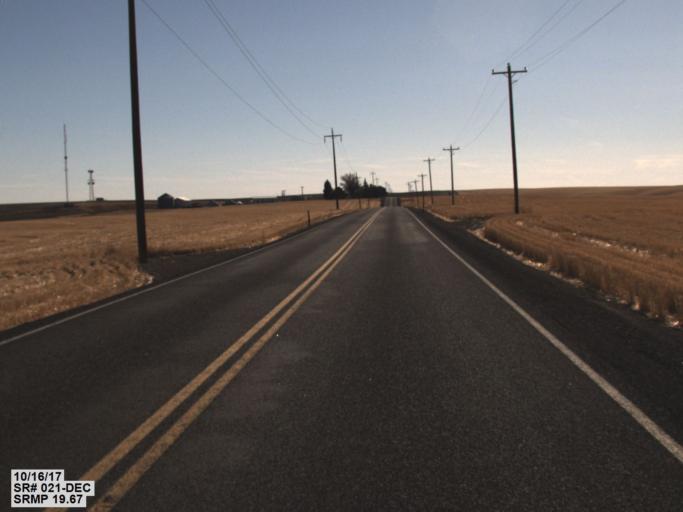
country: US
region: Washington
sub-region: Adams County
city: Ritzville
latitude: 46.9050
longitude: -118.5678
